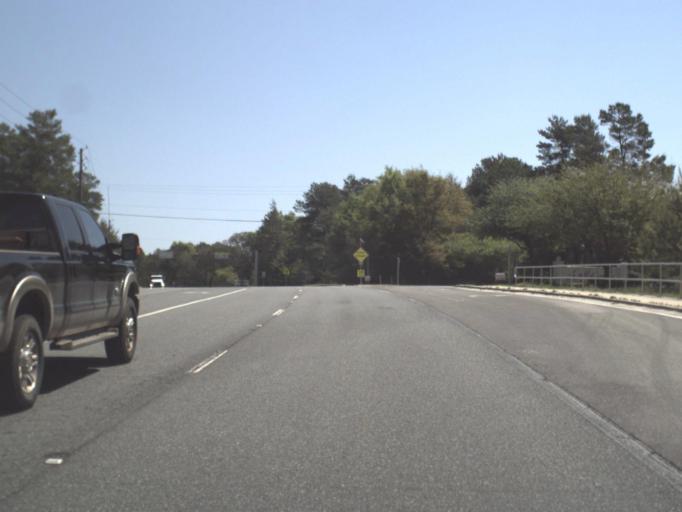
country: US
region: Florida
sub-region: Okaloosa County
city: Niceville
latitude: 30.5282
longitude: -86.4652
